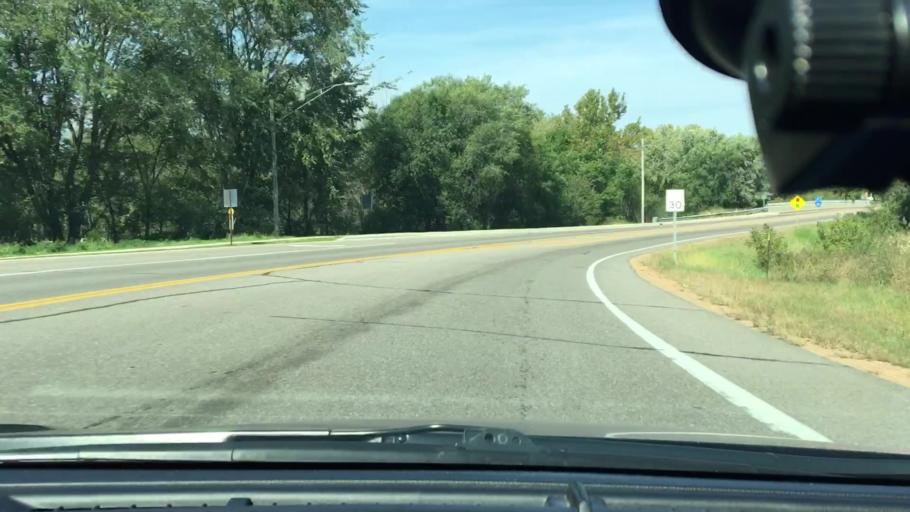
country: US
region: Minnesota
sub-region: Wright County
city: Hanover
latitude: 45.1531
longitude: -93.6658
